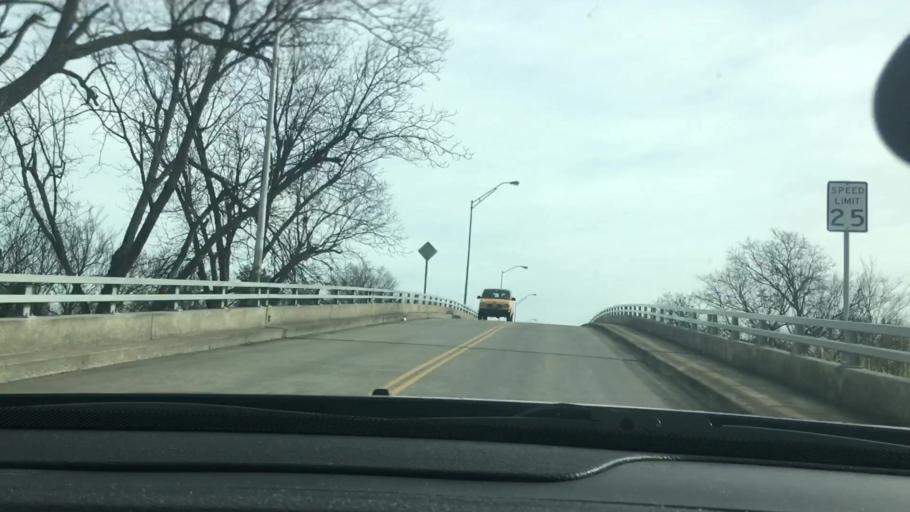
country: US
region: Oklahoma
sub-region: Carter County
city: Ardmore
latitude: 34.1775
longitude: -97.1243
